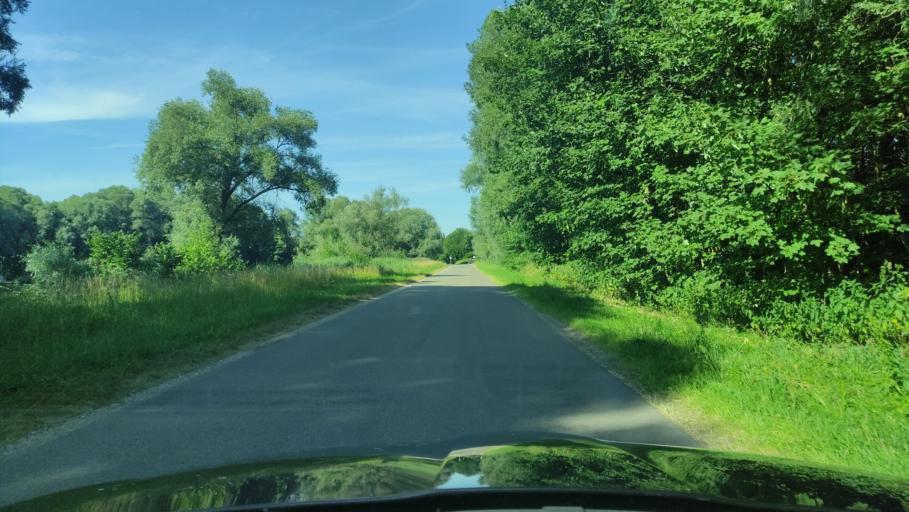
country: DE
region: Bavaria
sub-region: Swabia
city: Breitenthal
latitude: 48.2242
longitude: 10.2890
